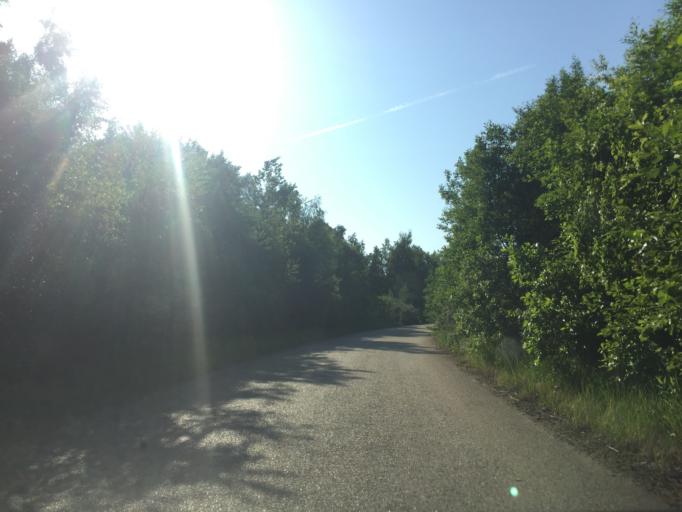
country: DK
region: Capital Region
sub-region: Kobenhavn
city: Copenhagen
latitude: 55.6302
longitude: 12.5505
